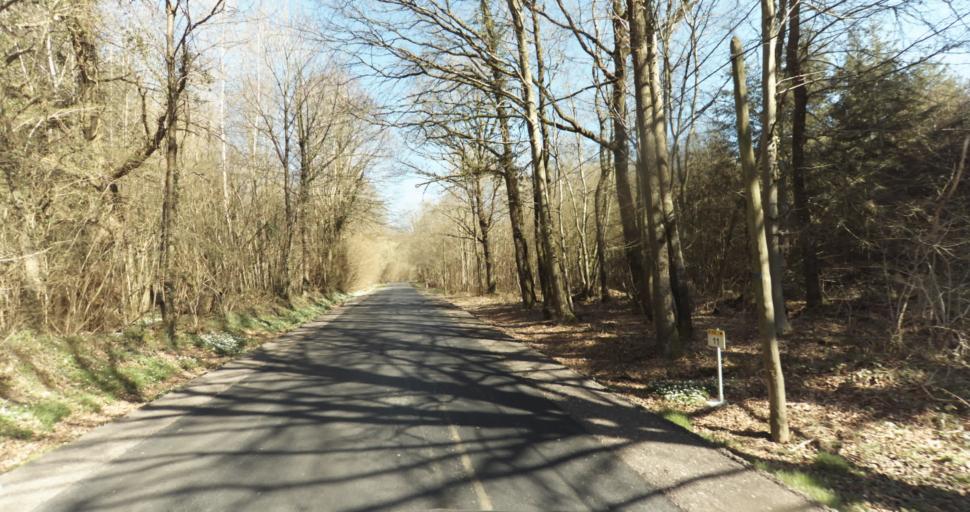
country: FR
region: Lower Normandy
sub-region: Departement de l'Orne
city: Trun
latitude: 48.9262
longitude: 0.0658
